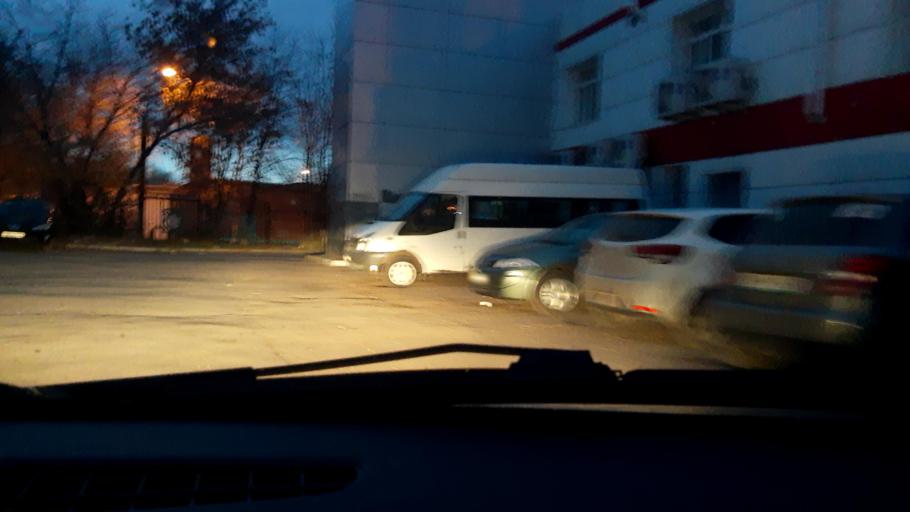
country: RU
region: Bashkortostan
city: Mikhaylovka
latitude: 54.7073
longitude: 55.8287
